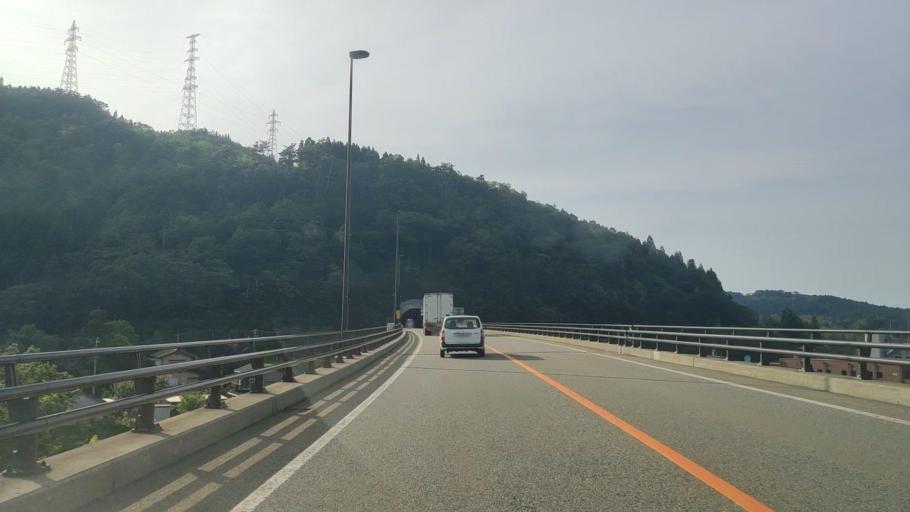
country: JP
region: Toyama
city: Yatsuomachi-higashikumisaka
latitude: 36.5262
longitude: 137.2296
